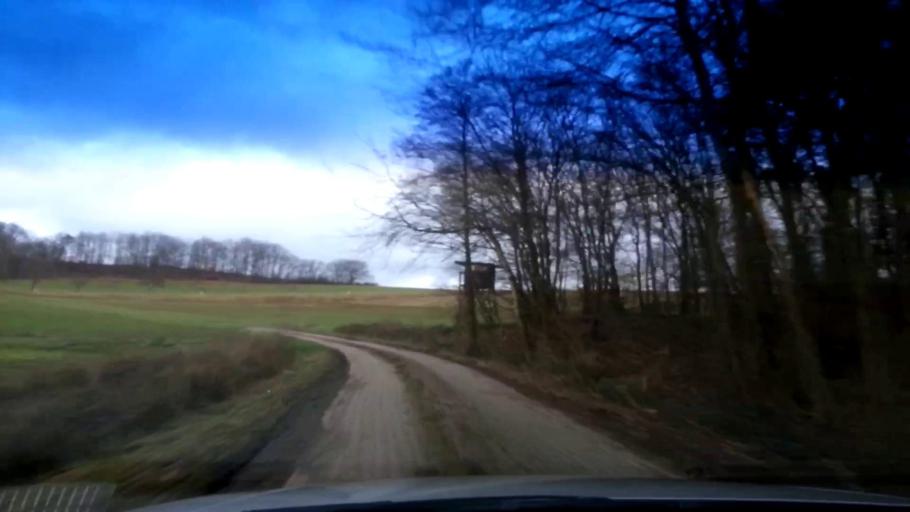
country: DE
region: Bavaria
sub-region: Upper Franconia
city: Schesslitz
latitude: 50.0100
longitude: 11.0315
